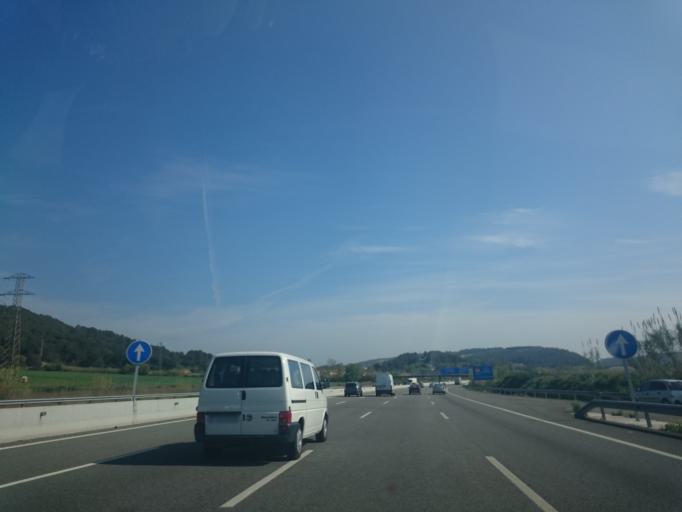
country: ES
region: Catalonia
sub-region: Provincia de Girona
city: Sarria de Ter
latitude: 42.0219
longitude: 2.8171
